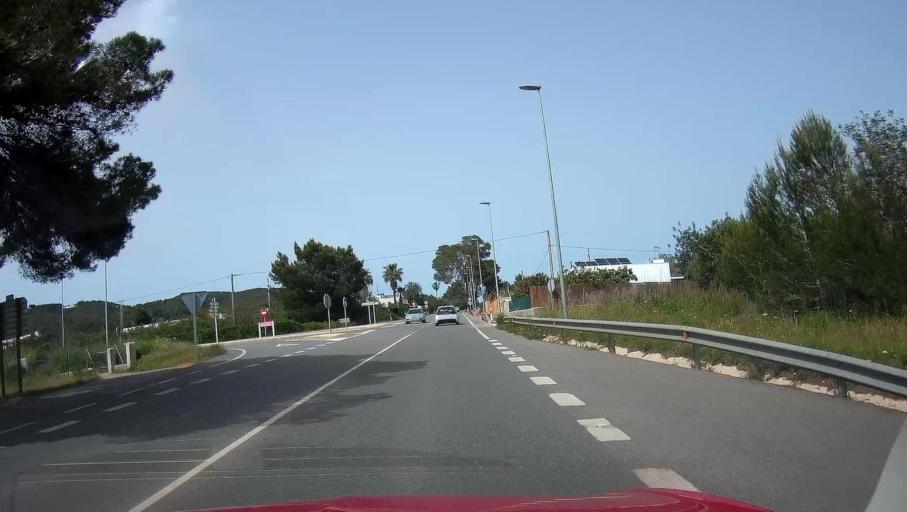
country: ES
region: Balearic Islands
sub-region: Illes Balears
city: Sant Joan de Labritja
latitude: 39.0265
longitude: 1.4874
